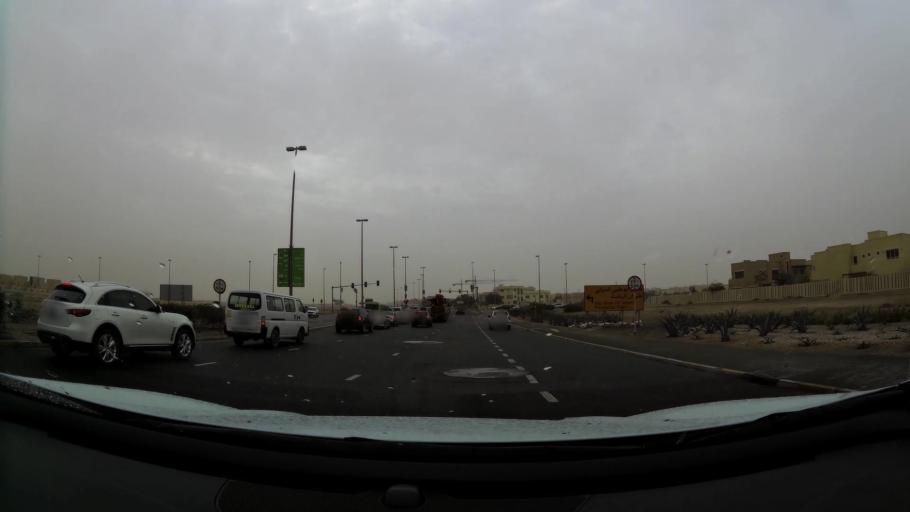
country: AE
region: Abu Dhabi
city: Abu Dhabi
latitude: 24.4422
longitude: 54.6012
